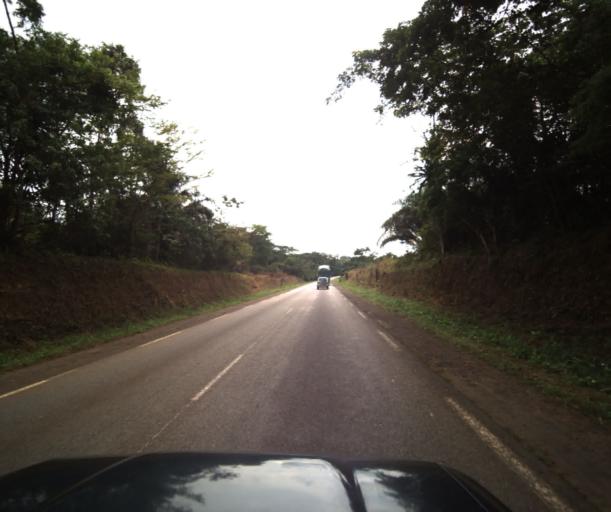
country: CM
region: Littoral
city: Edea
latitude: 3.8357
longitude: 10.4149
